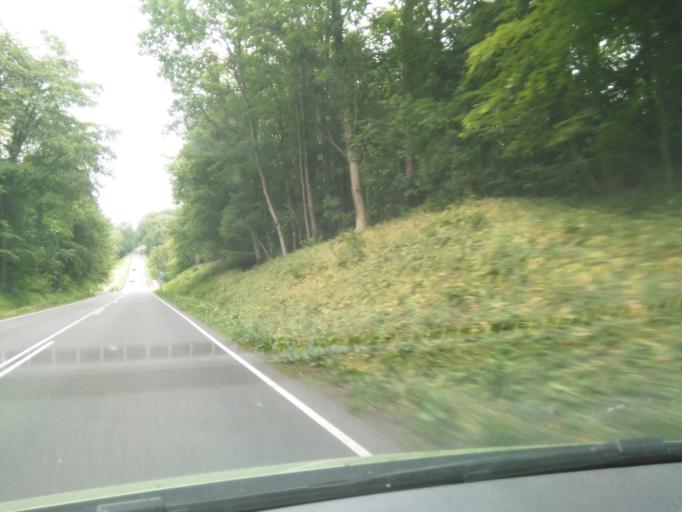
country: DK
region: Capital Region
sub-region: Bornholm Kommune
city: Akirkeby
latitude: 55.2286
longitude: 14.8816
